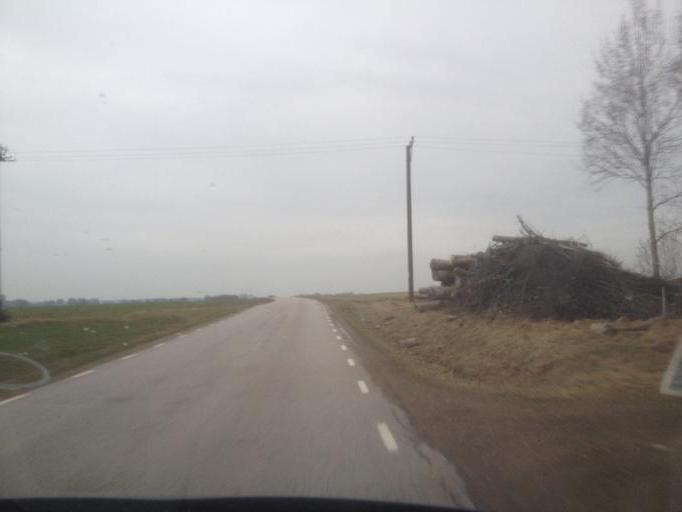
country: SE
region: OEstergoetland
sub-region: Linkopings Kommun
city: Vikingstad
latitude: 58.4241
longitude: 15.4645
